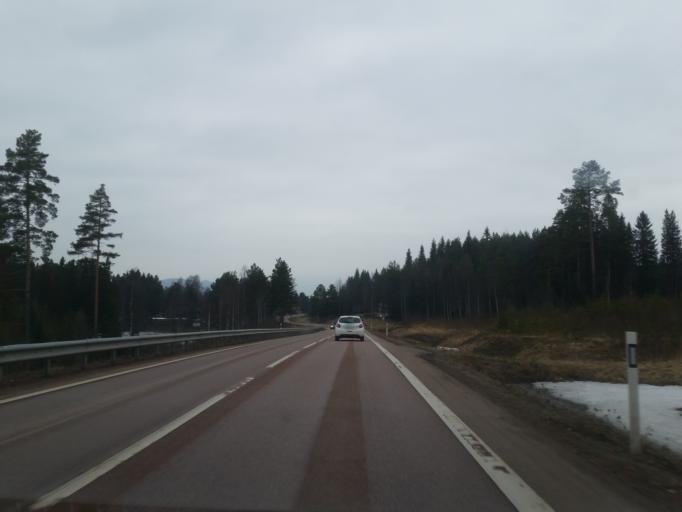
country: SE
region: Dalarna
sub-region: Alvdalens Kommun
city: AElvdalen
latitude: 61.2056
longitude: 14.0664
